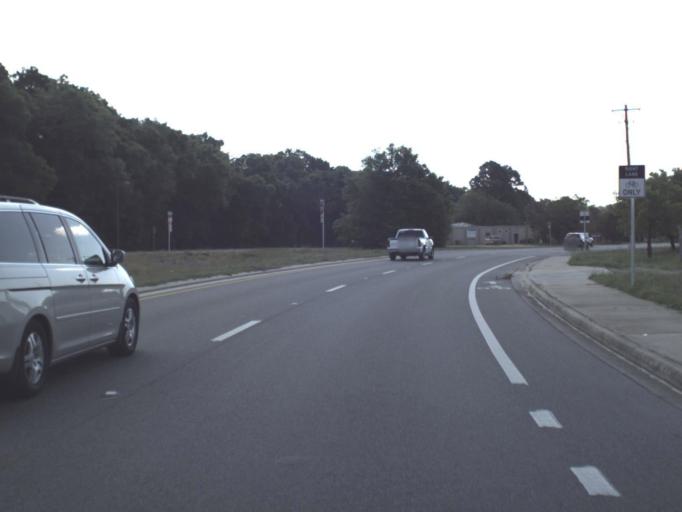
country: US
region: Florida
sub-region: Escambia County
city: Goulding
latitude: 30.4516
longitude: -87.2185
